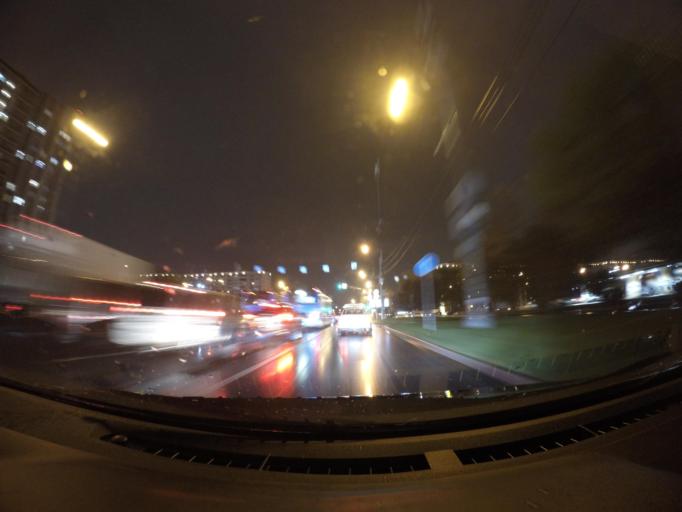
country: RU
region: Moscow
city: Orekhovo-Borisovo
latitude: 55.6018
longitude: 37.7242
